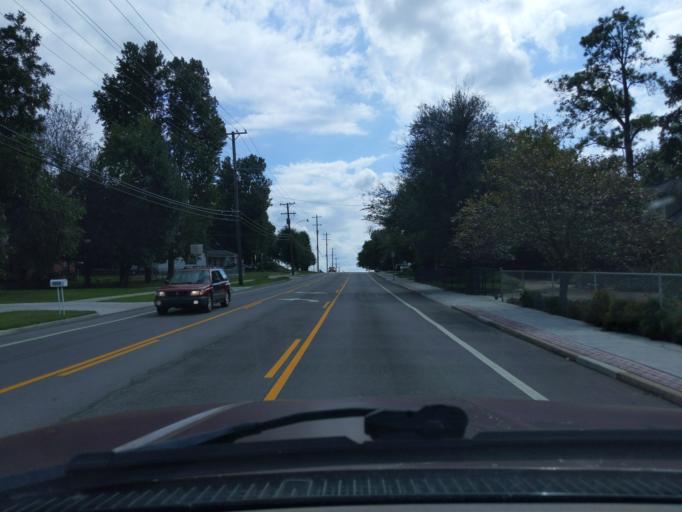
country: US
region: Oklahoma
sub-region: Tulsa County
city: Oakhurst
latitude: 36.0969
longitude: -96.0117
